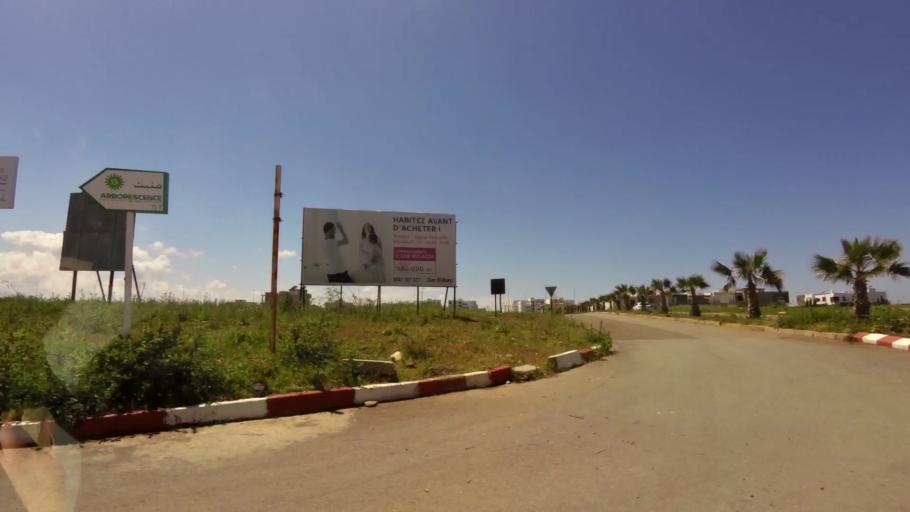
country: MA
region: Grand Casablanca
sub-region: Nouaceur
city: Dar Bouazza
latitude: 33.5262
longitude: -7.8196
